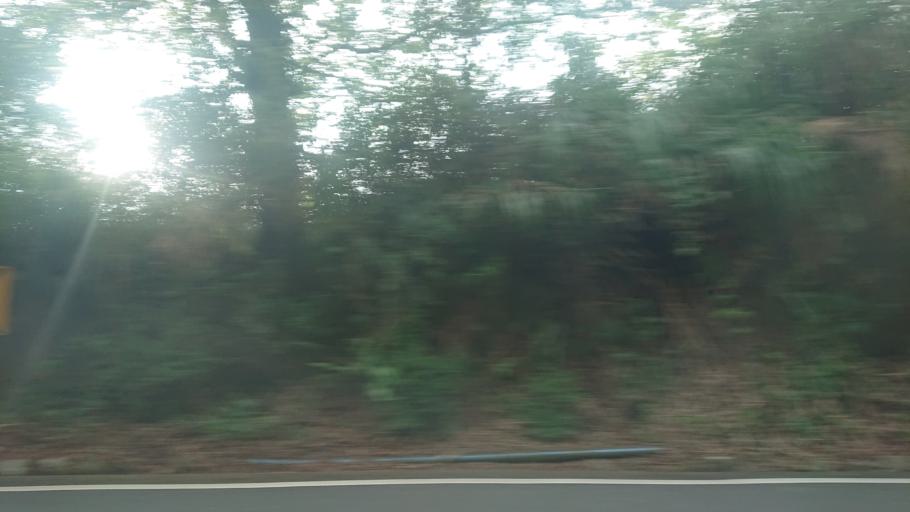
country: TW
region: Taiwan
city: Lugu
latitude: 23.4964
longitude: 120.7918
